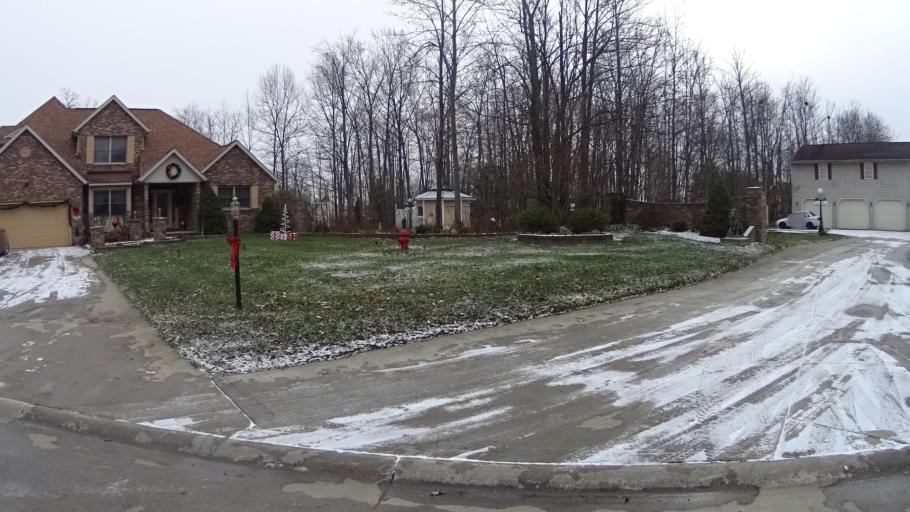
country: US
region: Ohio
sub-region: Lorain County
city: Lagrange
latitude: 41.2016
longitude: -82.1504
